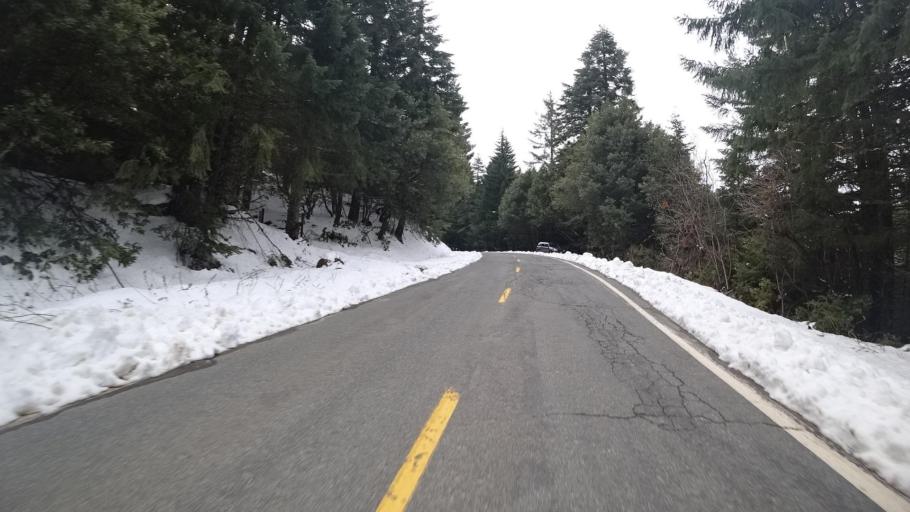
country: US
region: California
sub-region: Humboldt County
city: Willow Creek
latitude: 40.8675
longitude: -123.7422
